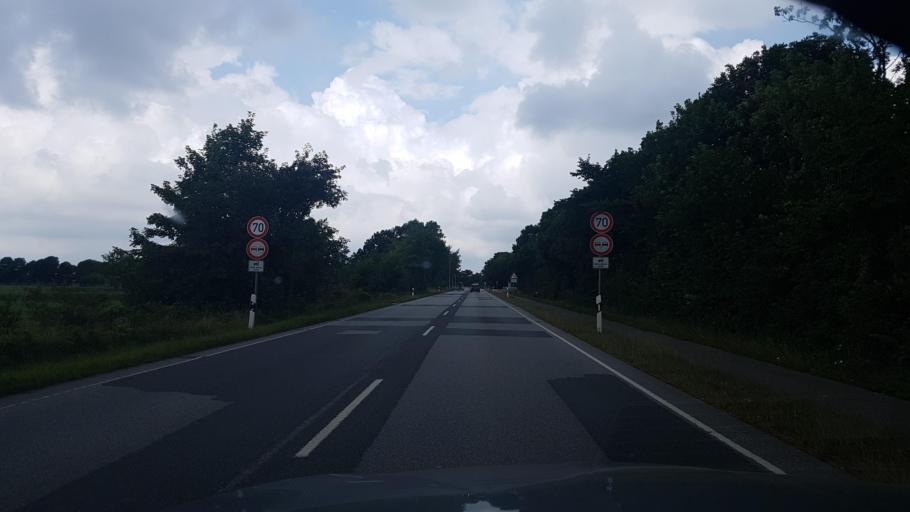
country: DE
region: Schleswig-Holstein
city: Husum
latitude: 54.4950
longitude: 9.0298
